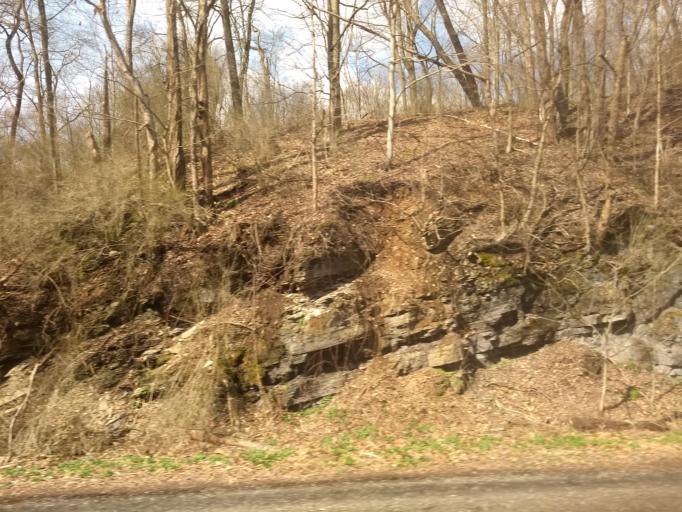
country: US
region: Pennsylvania
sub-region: Blair County
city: Tyrone
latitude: 40.6426
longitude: -78.1971
